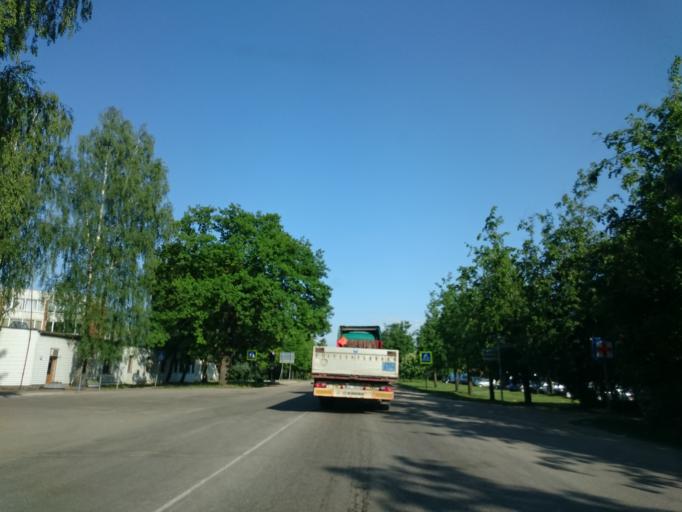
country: LV
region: Stopini
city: Ulbroka
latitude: 56.9429
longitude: 24.2838
